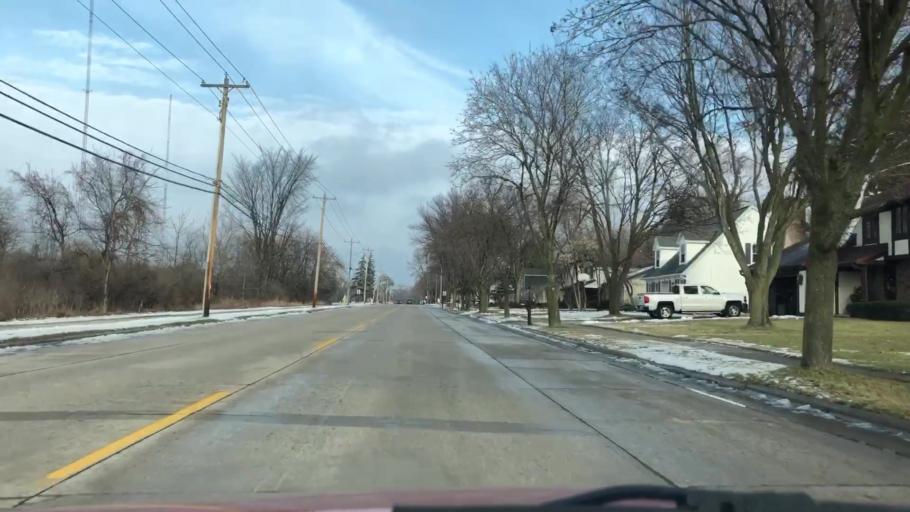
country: US
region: Wisconsin
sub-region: Brown County
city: De Pere
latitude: 44.4329
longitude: -88.0756
